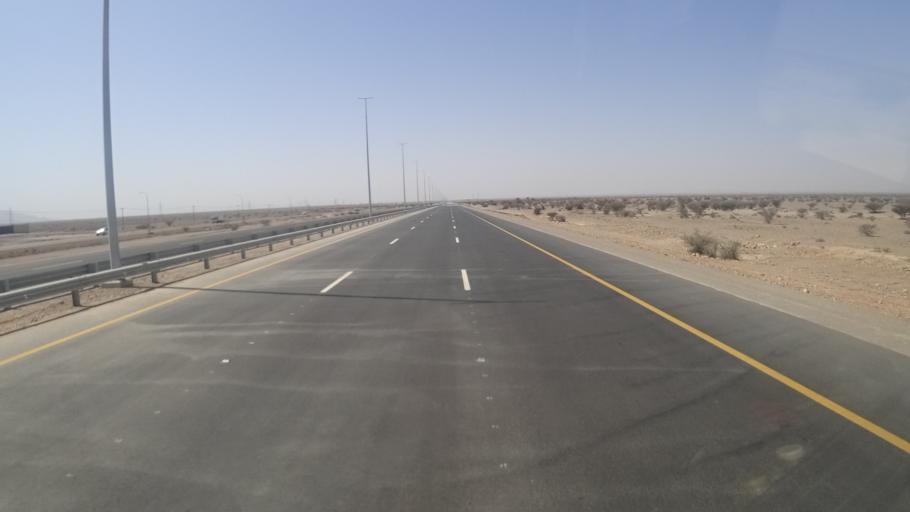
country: OM
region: Ash Sharqiyah
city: Sur
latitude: 22.3034
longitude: 59.2841
